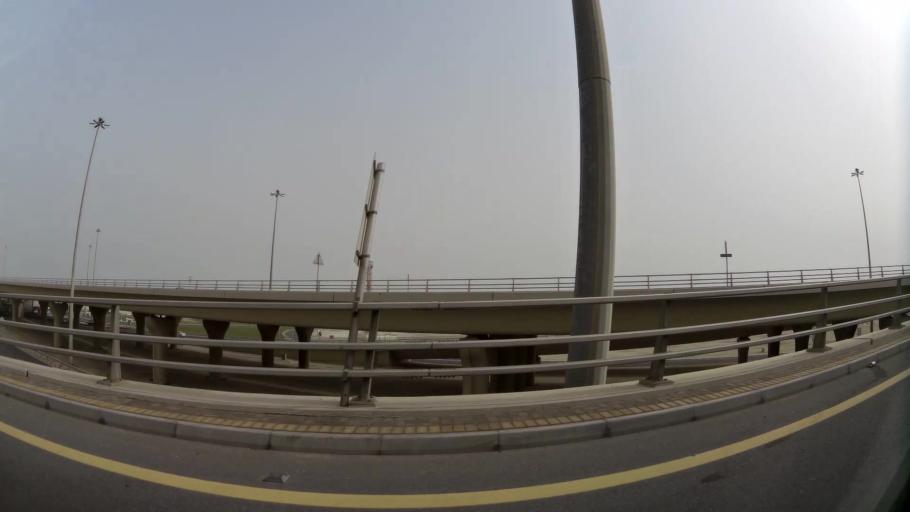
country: BH
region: Muharraq
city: Al Muharraq
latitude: 26.2449
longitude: 50.5910
